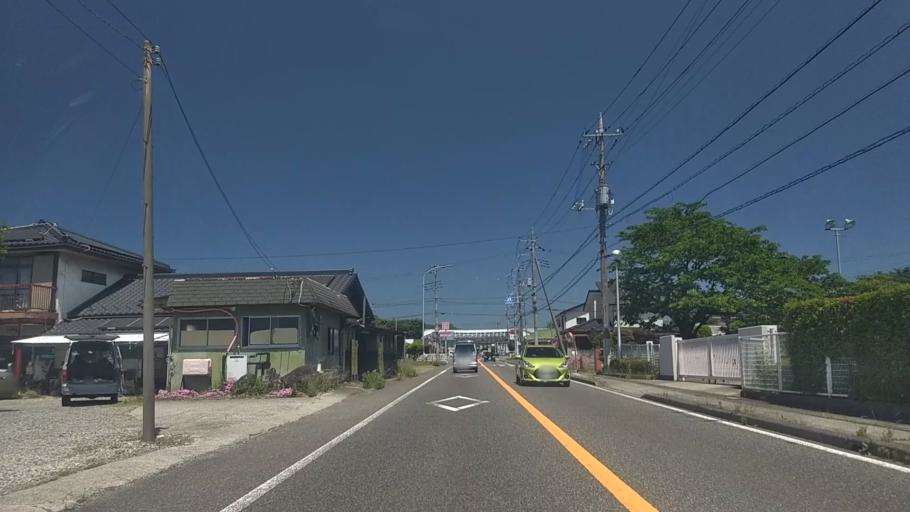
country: JP
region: Yamanashi
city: Nirasaki
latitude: 35.7462
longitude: 138.4399
